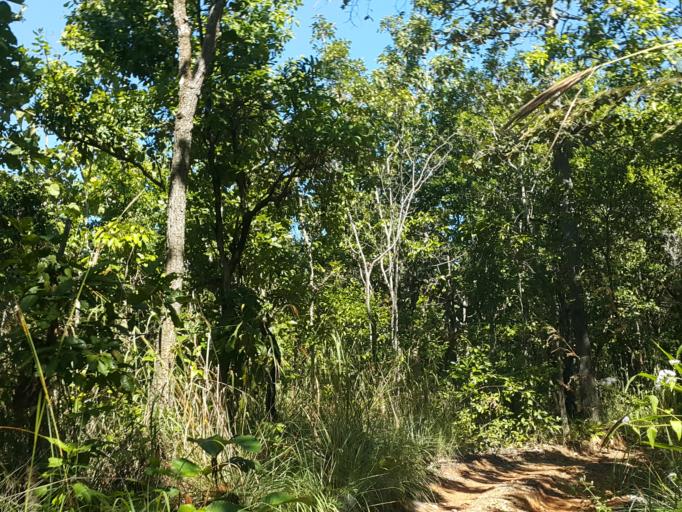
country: TH
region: Chiang Mai
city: Chiang Mai
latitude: 18.7989
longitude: 98.8662
